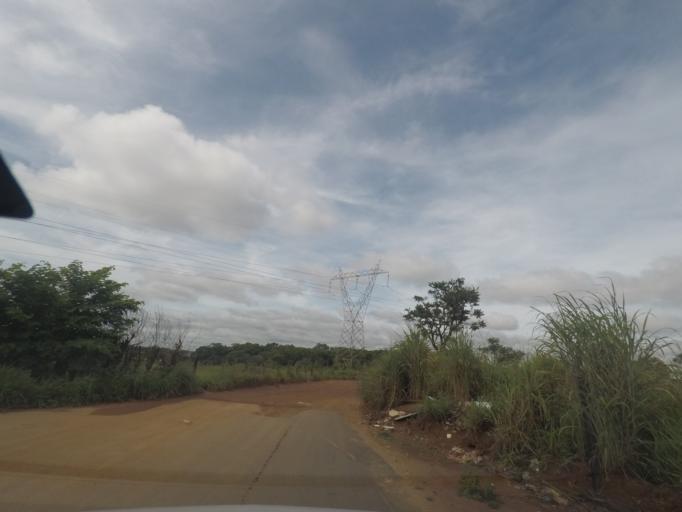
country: BR
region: Goias
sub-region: Goiania
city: Goiania
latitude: -16.6721
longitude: -49.1848
